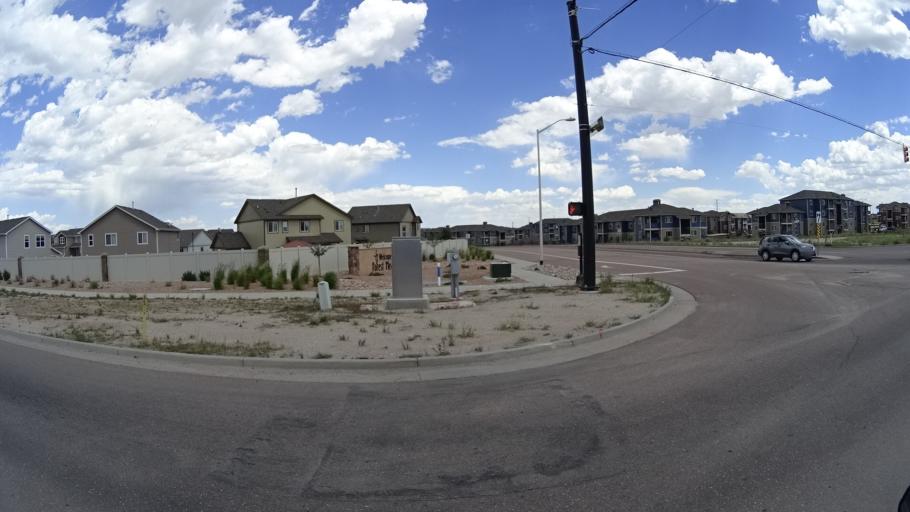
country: US
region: Colorado
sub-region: El Paso County
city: Black Forest
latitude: 38.9439
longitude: -104.7010
